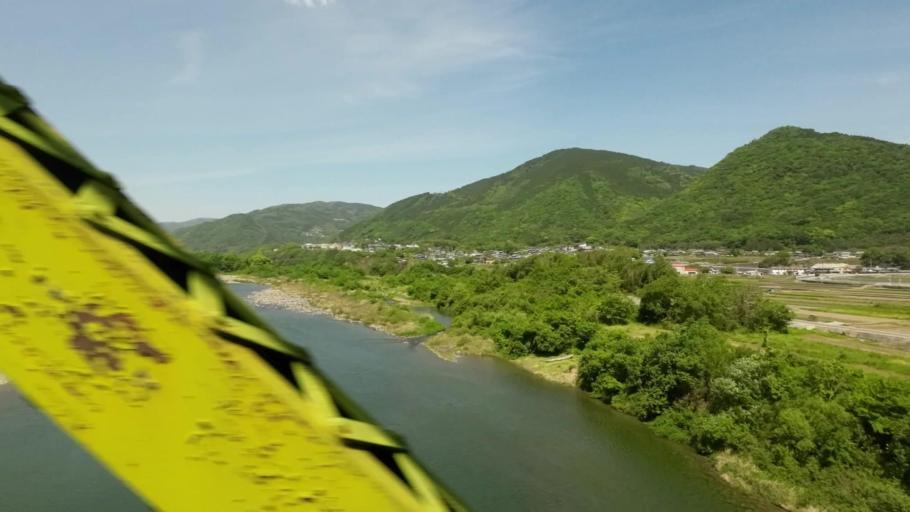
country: JP
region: Tokushima
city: Ikedacho
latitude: 34.0361
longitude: 133.8640
